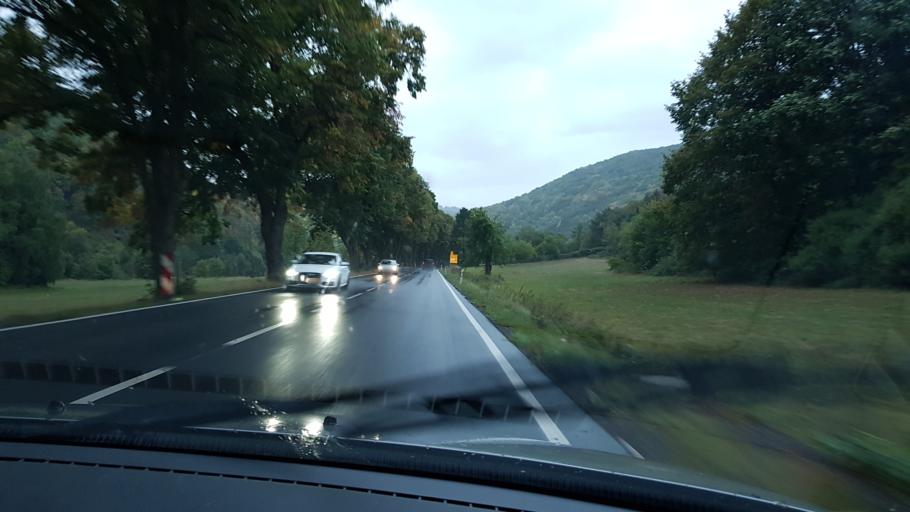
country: DE
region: Rheinland-Pfalz
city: Misselberg
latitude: 50.3172
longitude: 7.7678
